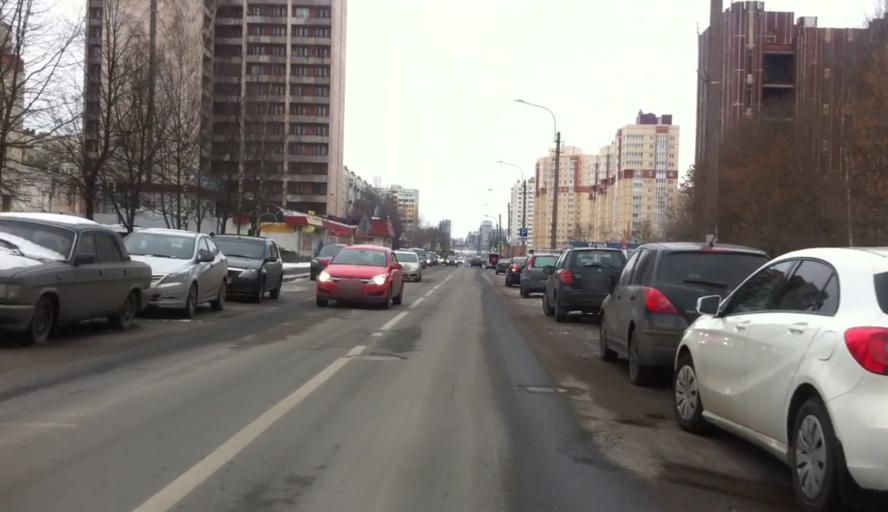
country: RU
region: St.-Petersburg
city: Uritsk
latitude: 59.8504
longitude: 30.1913
